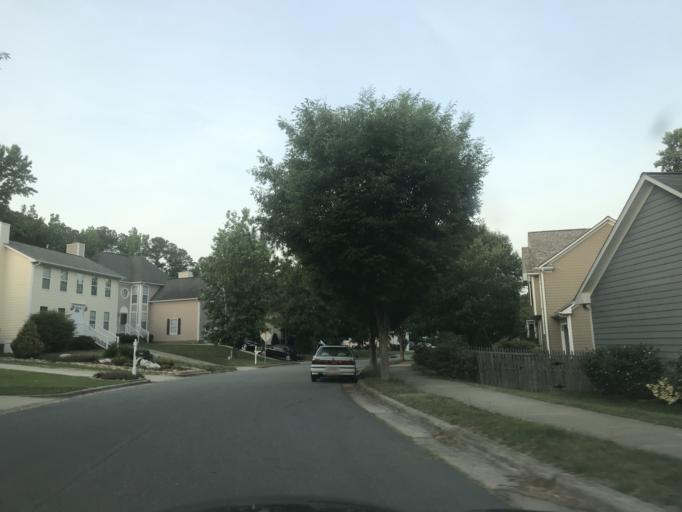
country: US
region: North Carolina
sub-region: Wake County
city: West Raleigh
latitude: 35.8820
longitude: -78.5959
